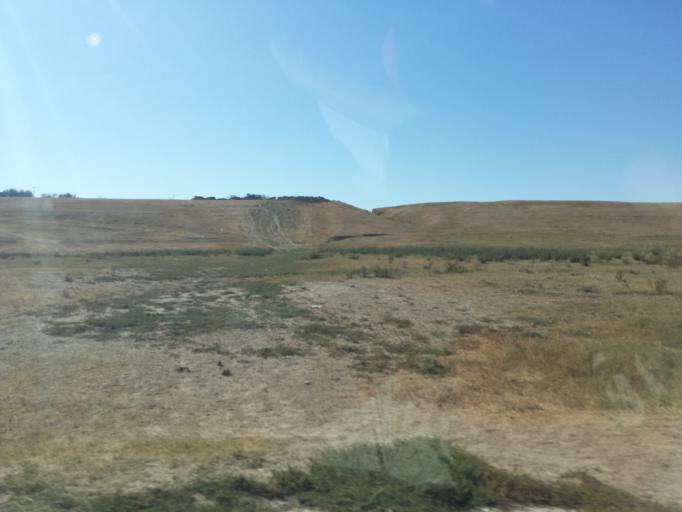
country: RO
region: Constanta
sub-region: Comuna Saraiu
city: Saraiu
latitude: 44.7272
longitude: 28.1662
